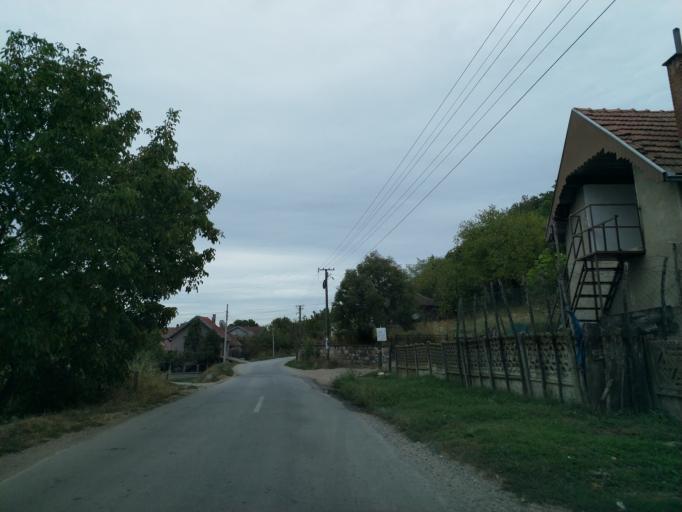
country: RS
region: Central Serbia
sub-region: Pomoravski Okrug
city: Cuprija
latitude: 43.8751
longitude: 21.3199
